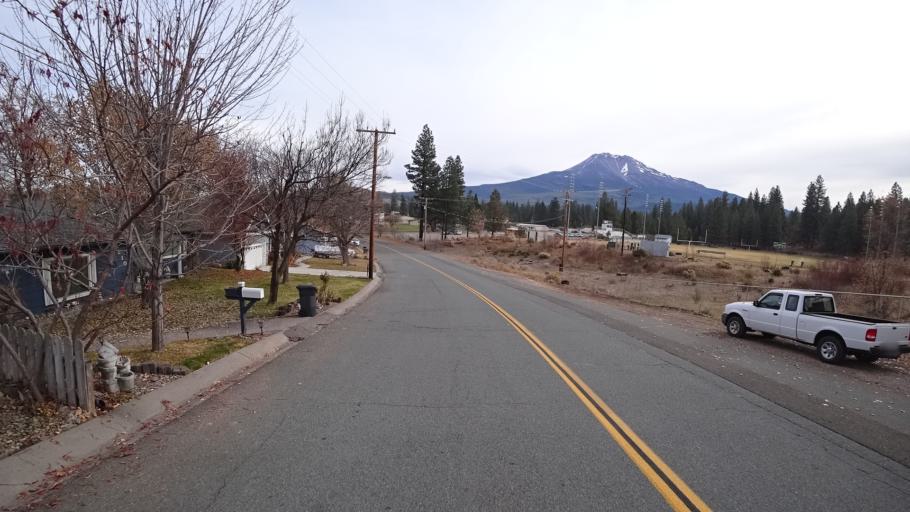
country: US
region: California
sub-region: Siskiyou County
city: Weed
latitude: 41.4274
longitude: -122.3762
